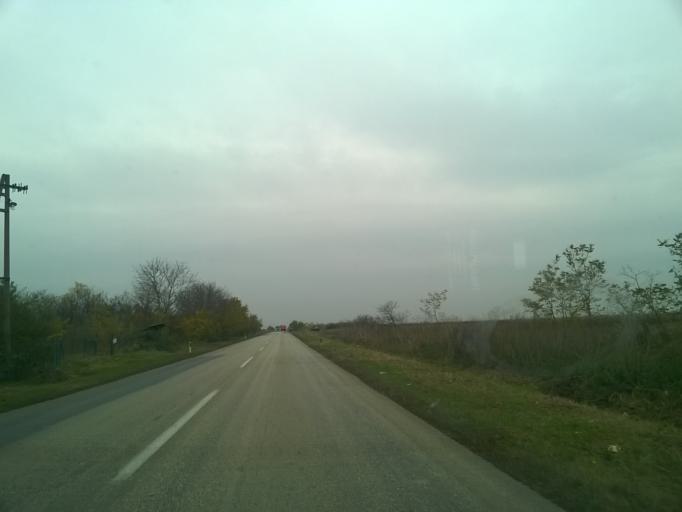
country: RS
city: Crepaja
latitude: 44.9471
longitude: 20.6660
